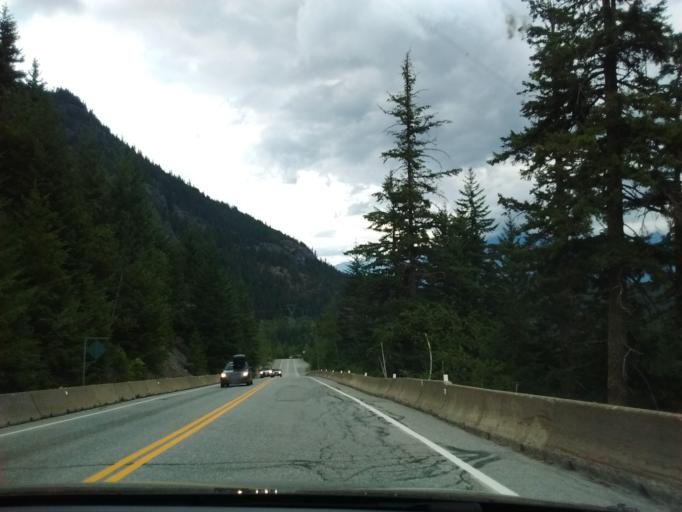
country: CA
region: British Columbia
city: Pemberton
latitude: 50.2890
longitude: -122.8367
